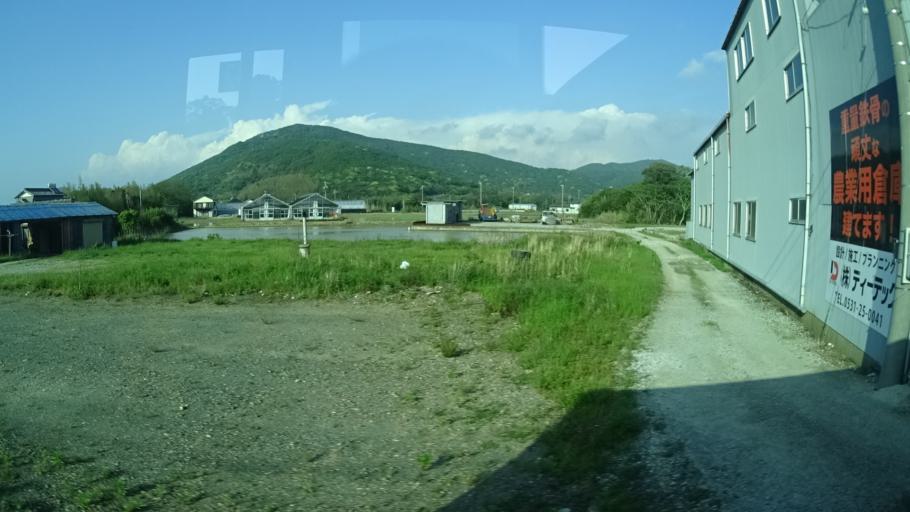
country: JP
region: Aichi
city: Tahara
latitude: 34.6591
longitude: 137.1982
